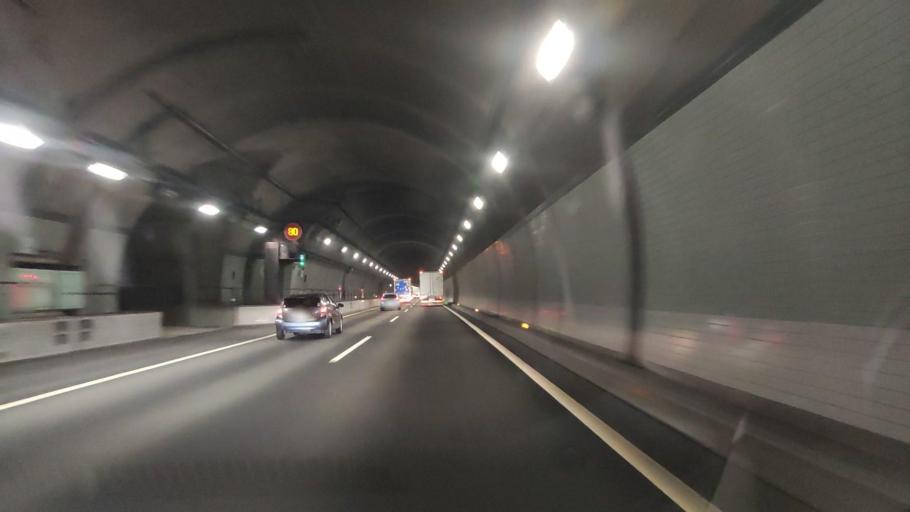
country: JP
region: Tokyo
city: Fussa
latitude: 35.7042
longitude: 139.2738
